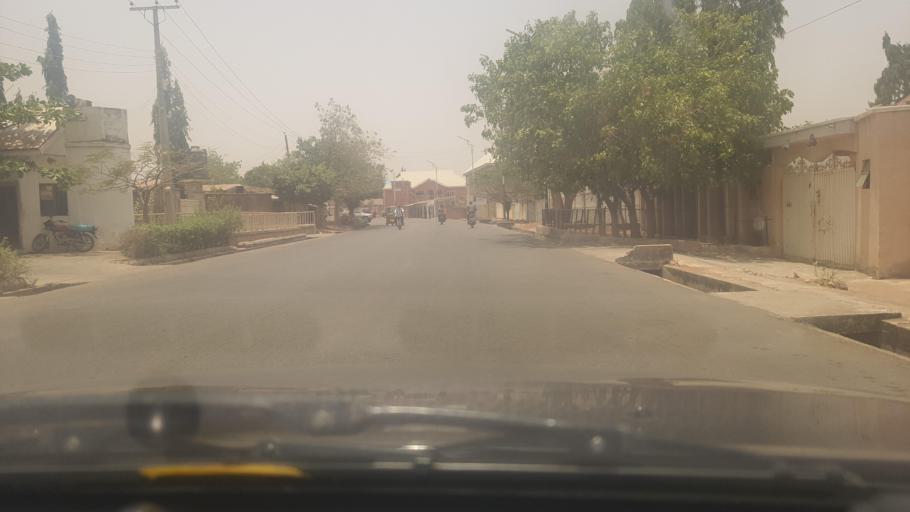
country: NG
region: Gombe
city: Gombe
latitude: 10.2975
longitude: 11.1520
